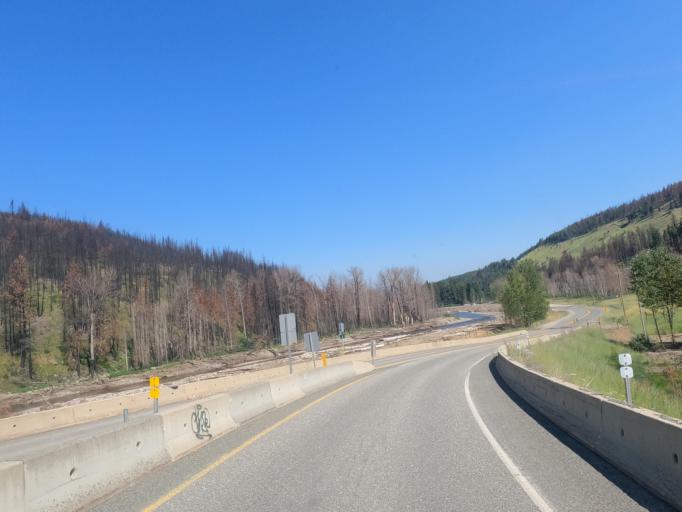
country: CA
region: British Columbia
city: Merritt
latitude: 49.8831
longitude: -120.9036
